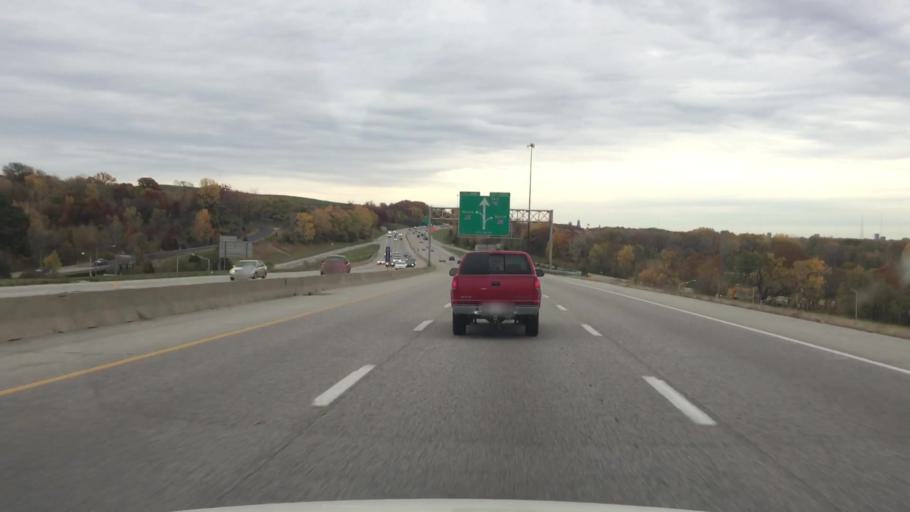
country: US
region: Kansas
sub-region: Johnson County
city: Shawnee
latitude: 39.1050
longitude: -94.7120
